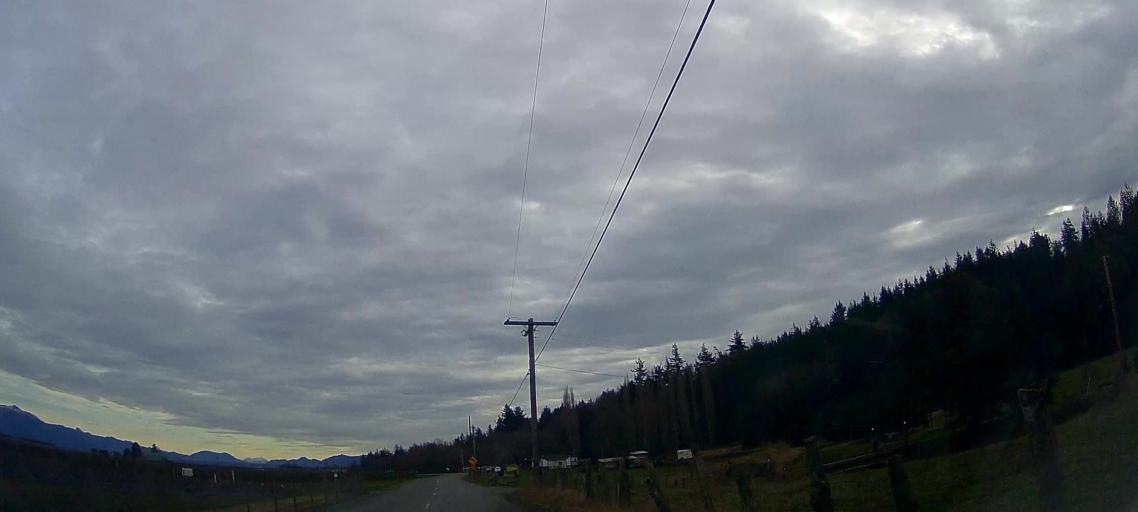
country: US
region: Washington
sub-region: Skagit County
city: Burlington
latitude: 48.5054
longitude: -122.4227
